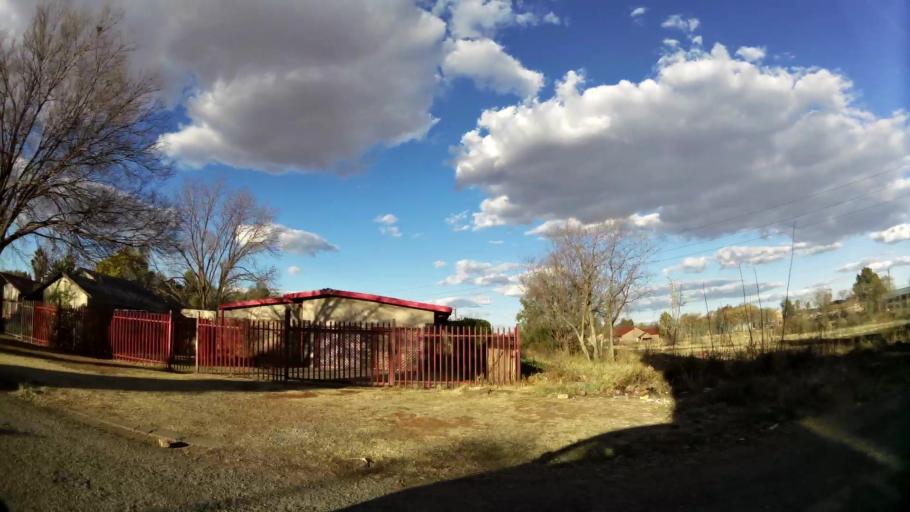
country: ZA
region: North-West
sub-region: Dr Kenneth Kaunda District Municipality
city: Potchefstroom
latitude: -26.7037
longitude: 27.0867
